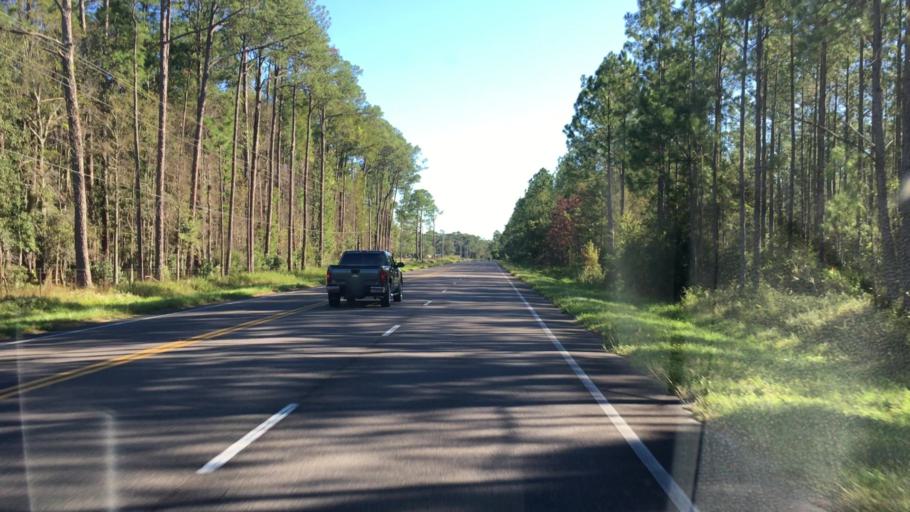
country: US
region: Florida
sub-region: Alachua County
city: Gainesville
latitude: 29.7487
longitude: -82.2776
